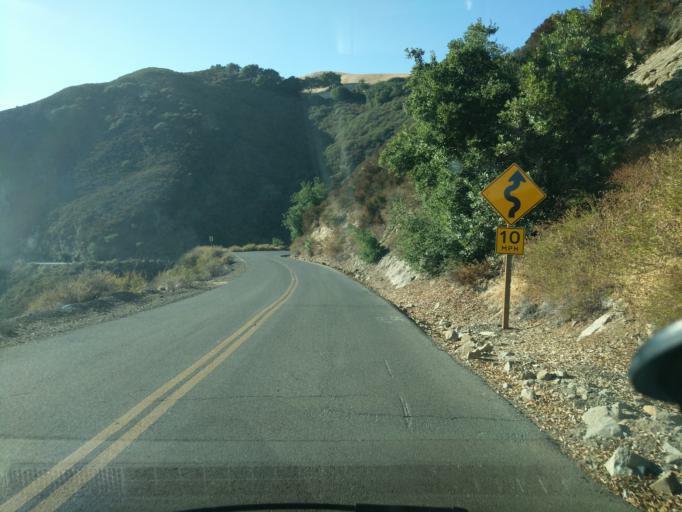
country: US
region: California
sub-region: Contra Costa County
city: Blackhawk
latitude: 37.8416
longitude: -121.9252
